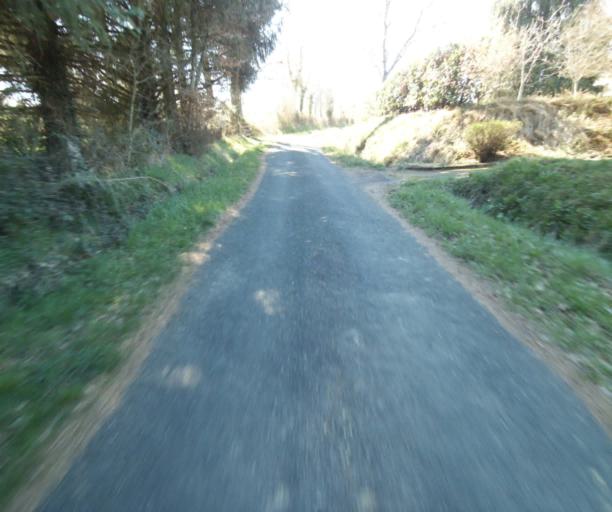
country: FR
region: Limousin
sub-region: Departement de la Correze
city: Chamboulive
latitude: 45.4278
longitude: 1.7062
